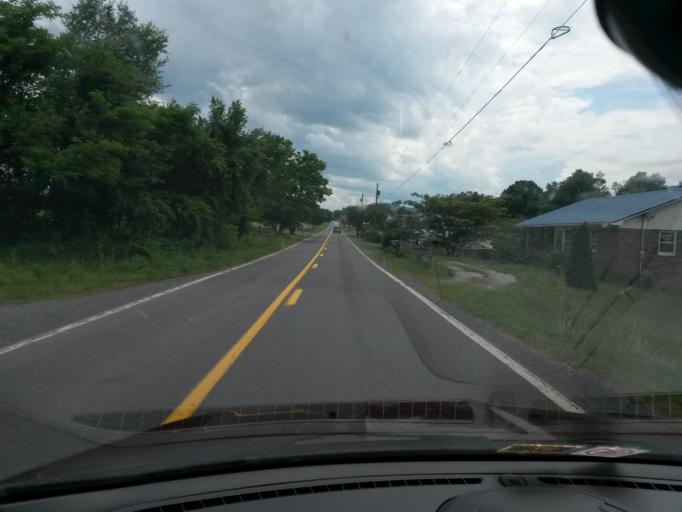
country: US
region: West Virginia
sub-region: Pendleton County
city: Franklin
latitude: 38.8128
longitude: -79.2669
